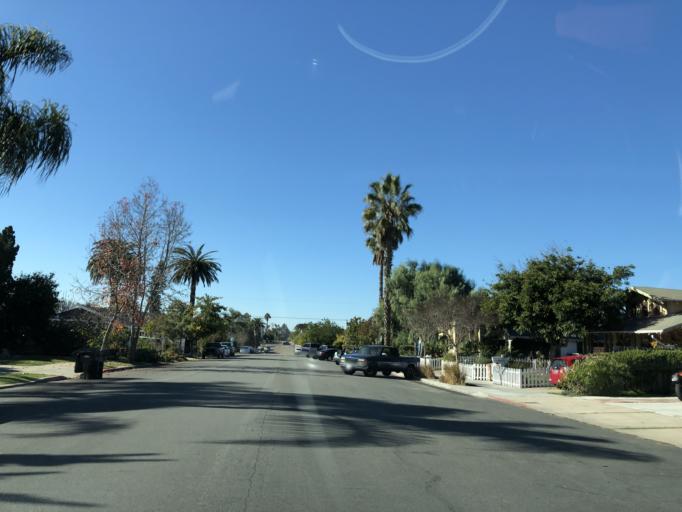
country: US
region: California
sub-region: San Diego County
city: San Diego
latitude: 32.7275
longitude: -117.1264
